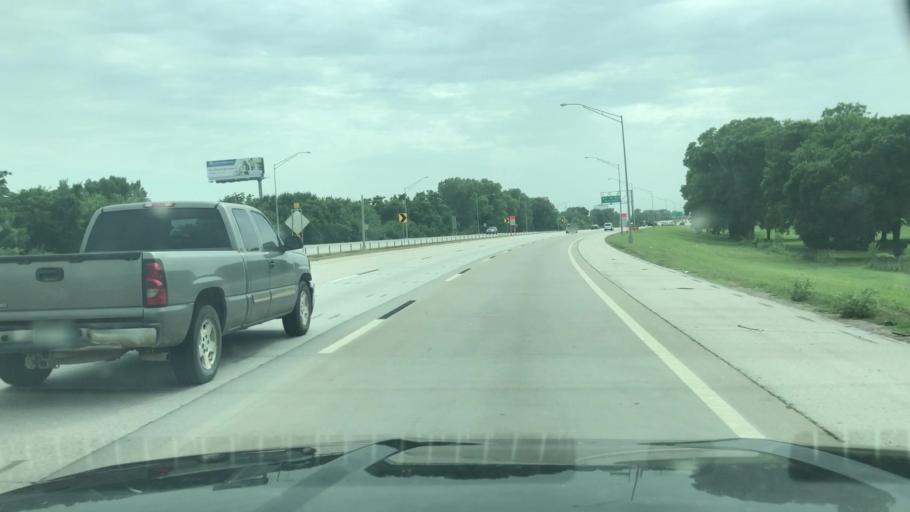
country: US
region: Oklahoma
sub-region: Tulsa County
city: Sand Springs
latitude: 36.1464
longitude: -96.0735
